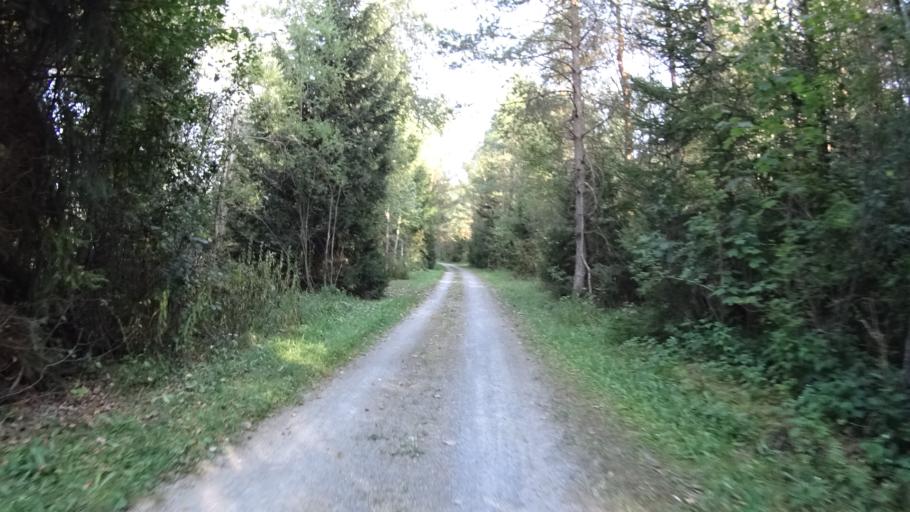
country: AT
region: Carinthia
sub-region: Politischer Bezirk Villach Land
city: Rosegg
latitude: 46.5725
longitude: 14.0503
